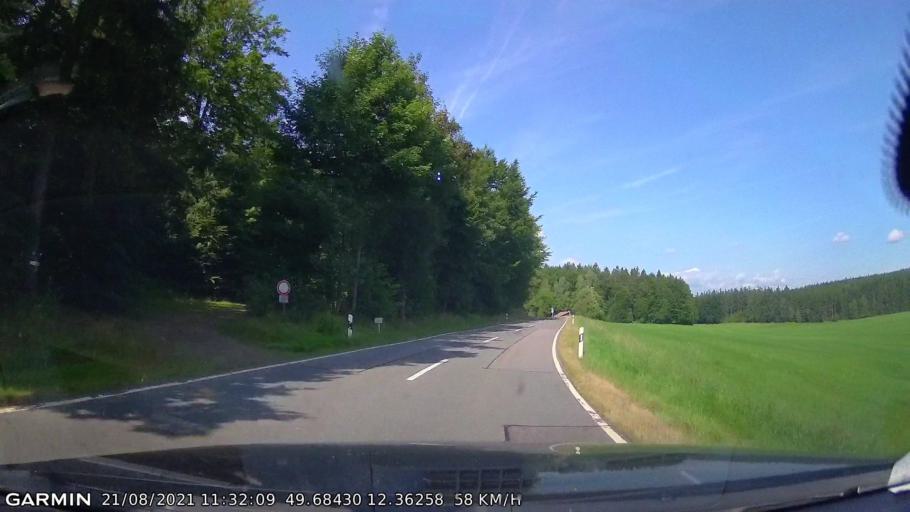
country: DE
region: Bavaria
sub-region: Upper Palatinate
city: Waldthurn
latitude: 49.6845
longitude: 12.3622
